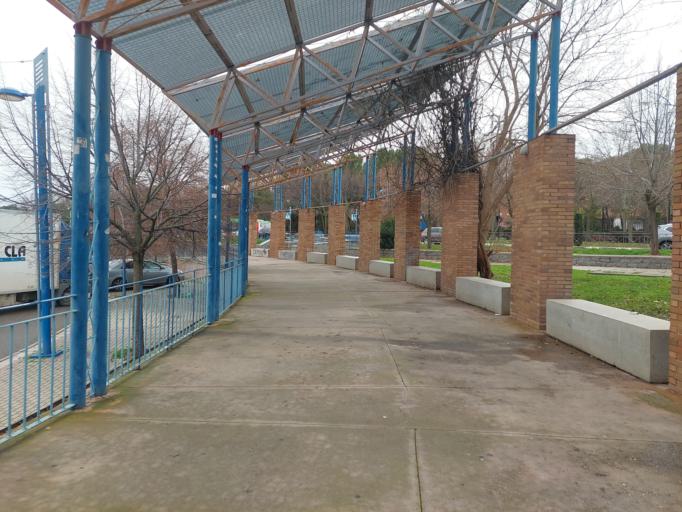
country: ES
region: Madrid
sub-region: Provincia de Madrid
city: Leganes
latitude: 40.3252
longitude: -3.7599
